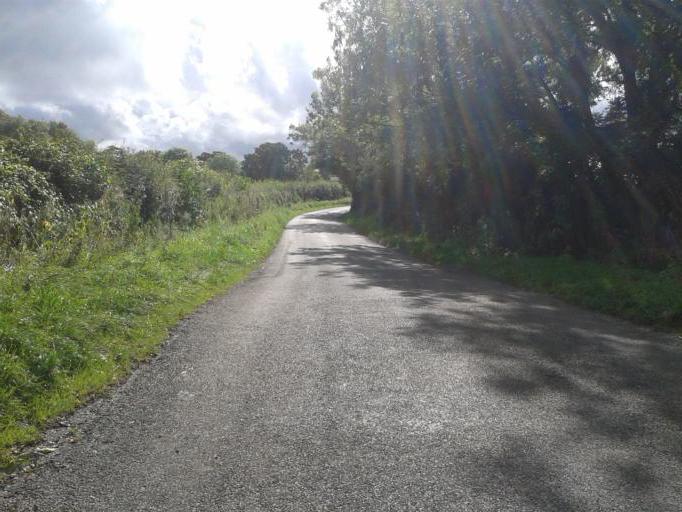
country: GB
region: England
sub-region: Hertfordshire
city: Buntingford
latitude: 51.9739
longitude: 0.0914
